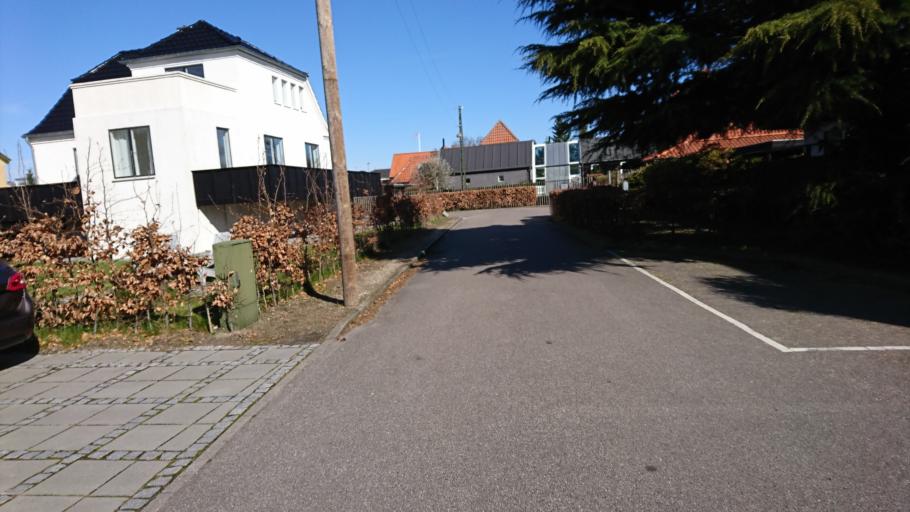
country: DK
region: Capital Region
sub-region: Dragor Kommune
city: Dragor
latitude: 55.5957
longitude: 12.6725
